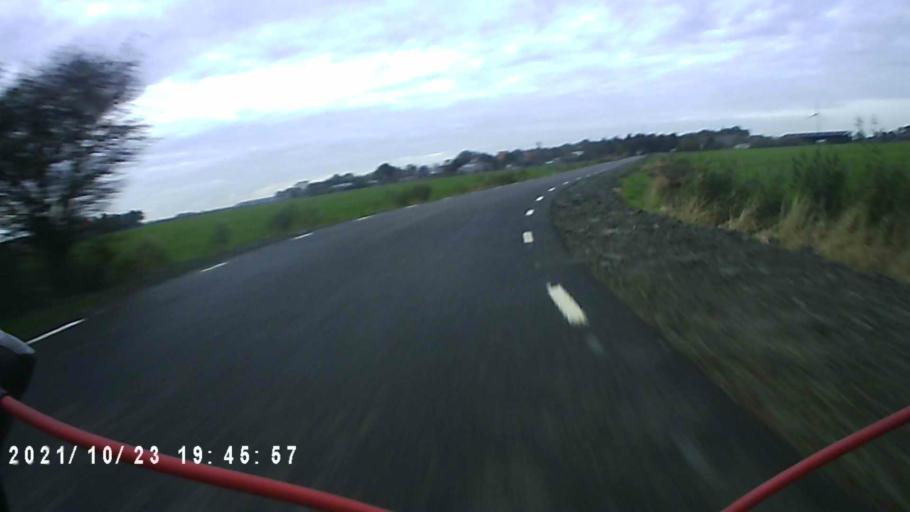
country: NL
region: Friesland
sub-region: Sudwest Fryslan
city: Makkum
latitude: 53.0799
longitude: 5.4270
